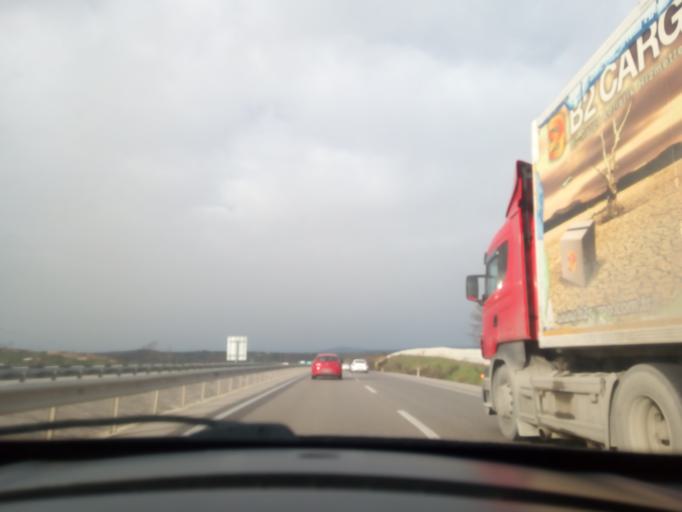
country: TR
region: Bursa
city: Mahmudiye
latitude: 40.2134
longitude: 28.6768
